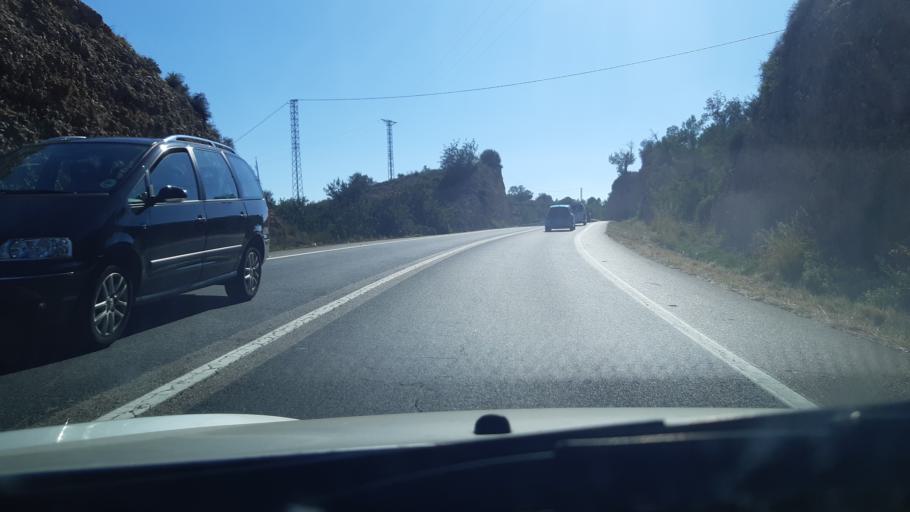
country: ES
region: Catalonia
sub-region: Provincia de Tarragona
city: Tivenys
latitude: 40.8806
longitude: 0.4976
